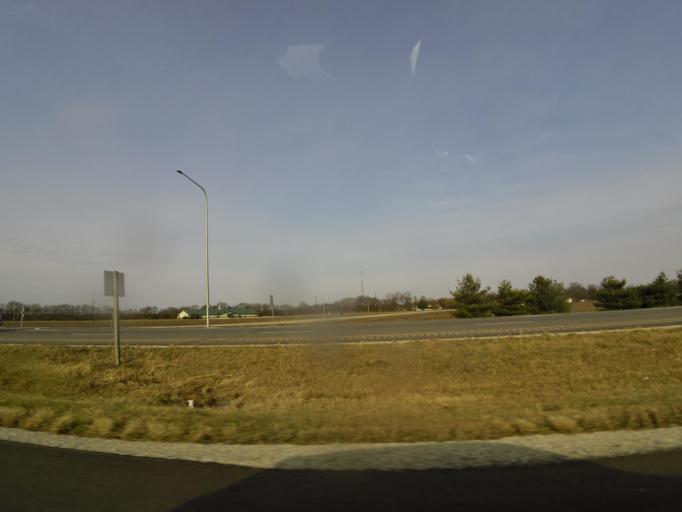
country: US
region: Illinois
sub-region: Shelby County
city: Moweaqua
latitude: 39.6140
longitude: -89.0188
